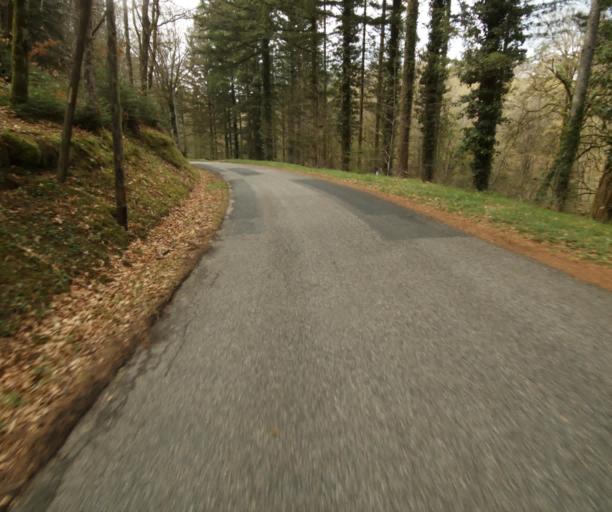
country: FR
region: Limousin
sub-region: Departement de la Correze
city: Argentat
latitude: 45.2026
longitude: 1.9633
